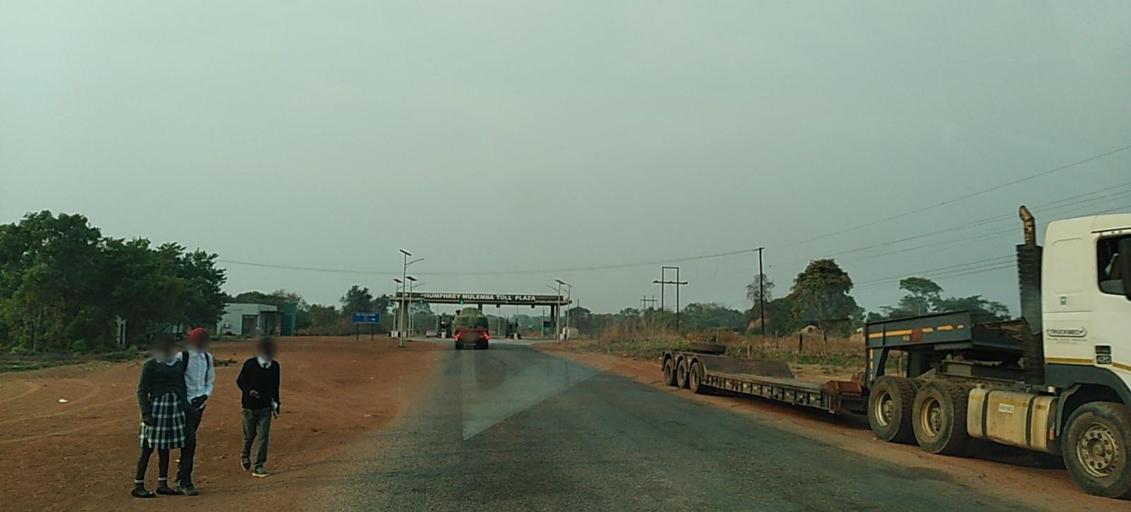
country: ZM
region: North-Western
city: Solwezi
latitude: -12.3154
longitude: 26.2702
